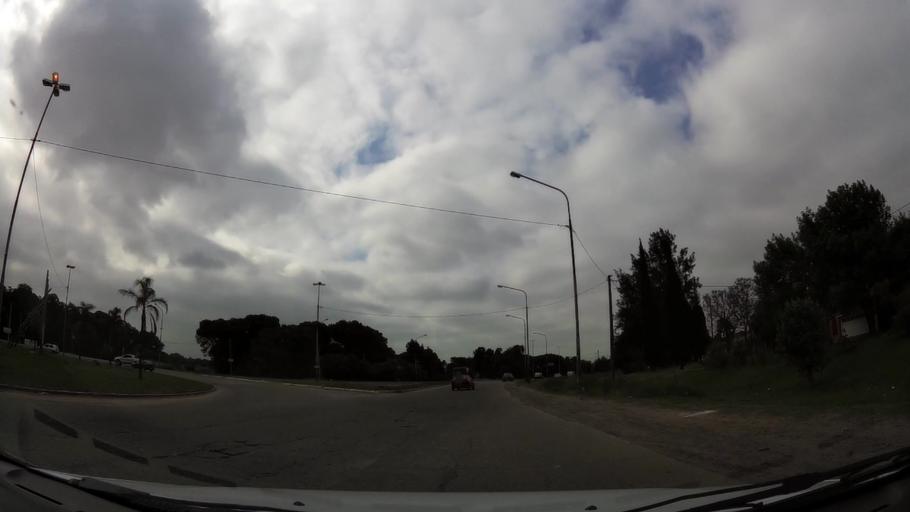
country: AR
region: Buenos Aires
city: San Justo
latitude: -34.7225
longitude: -58.5351
